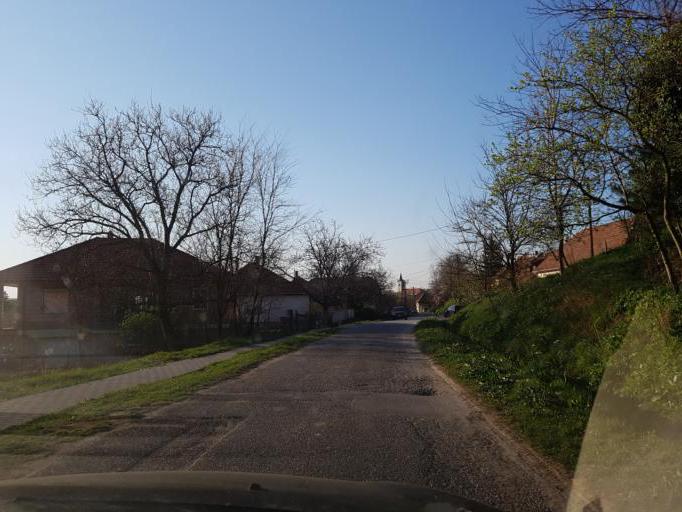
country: HU
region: Komarom-Esztergom
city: Piliscsev
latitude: 47.6751
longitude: 18.8228
